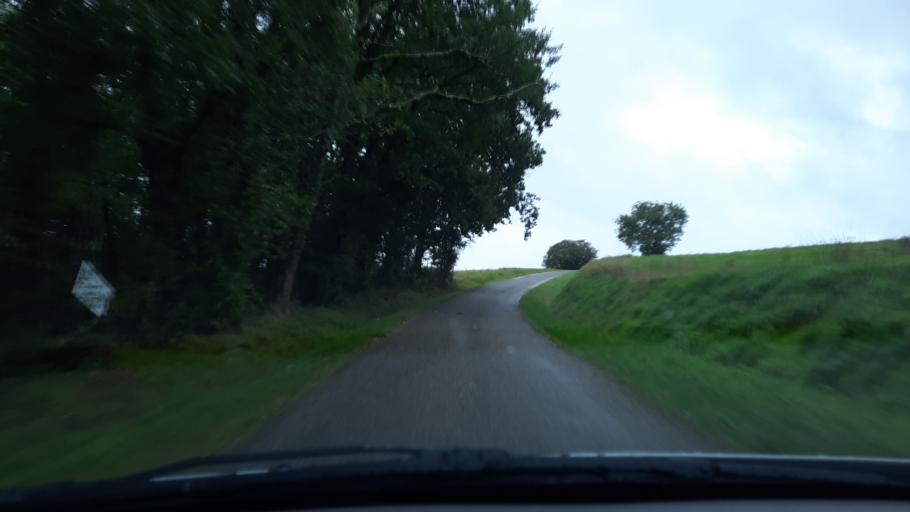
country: FR
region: Midi-Pyrenees
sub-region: Departement du Tarn-et-Garonne
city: Molieres
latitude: 44.1845
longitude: 1.3035
